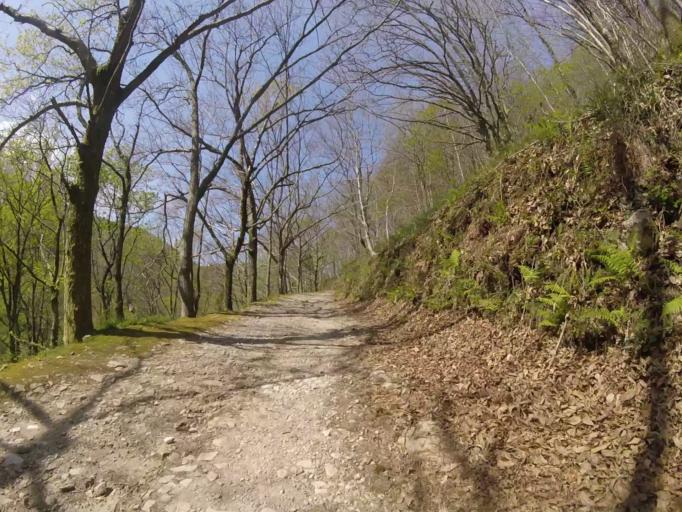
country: ES
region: Basque Country
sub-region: Provincia de Guipuzcoa
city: Irun
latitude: 43.2695
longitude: -1.8075
